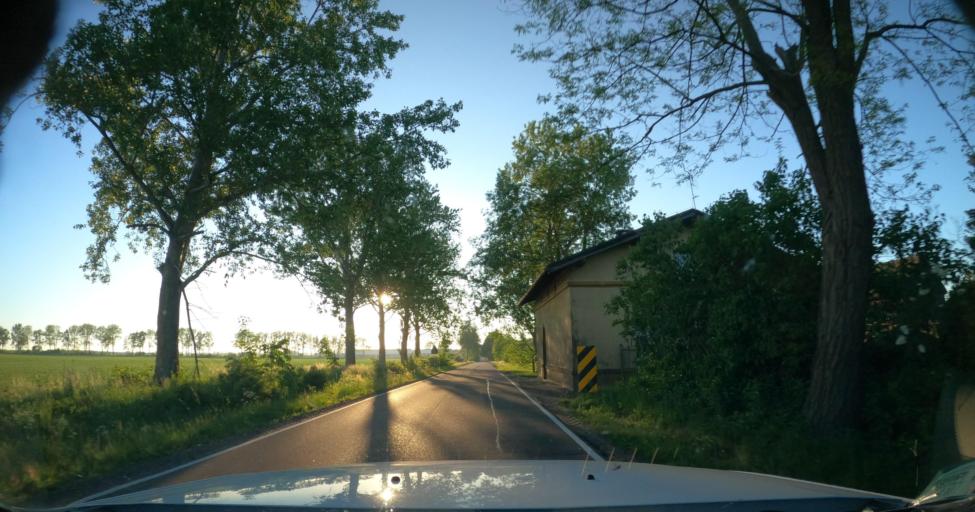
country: PL
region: Pomeranian Voivodeship
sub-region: Powiat slupski
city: Potegowo
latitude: 54.4093
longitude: 17.4221
